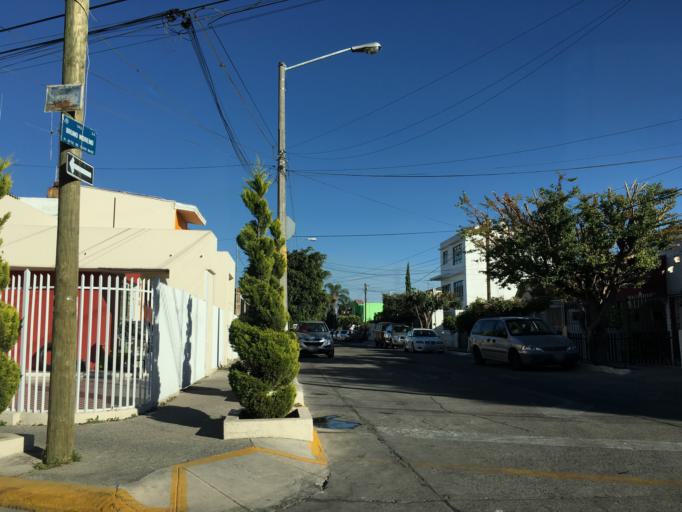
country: MX
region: Jalisco
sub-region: Zapopan
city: Zapopan
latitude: 20.7081
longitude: -103.3440
